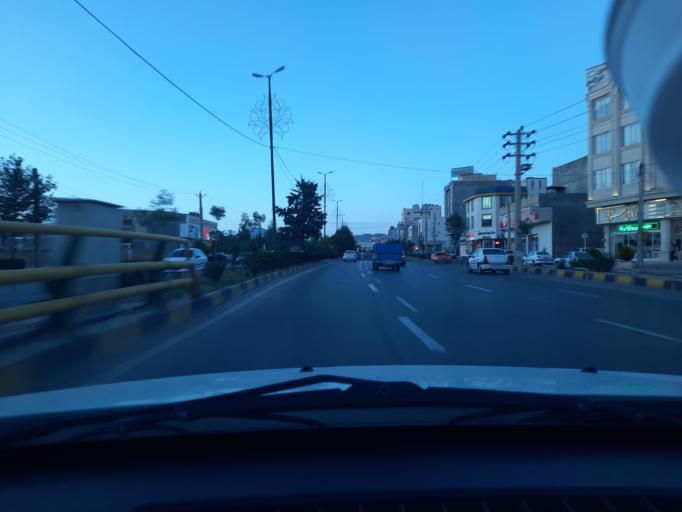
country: IR
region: Qazvin
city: Qazvin
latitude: 36.3053
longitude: 50.0113
